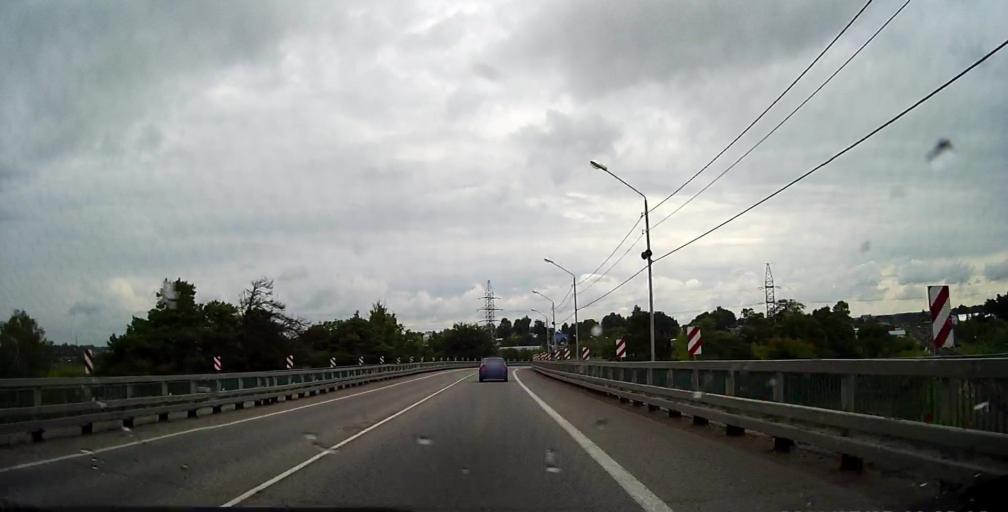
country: RU
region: Smolensk
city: Katyn'
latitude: 54.7834
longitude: 31.8258
